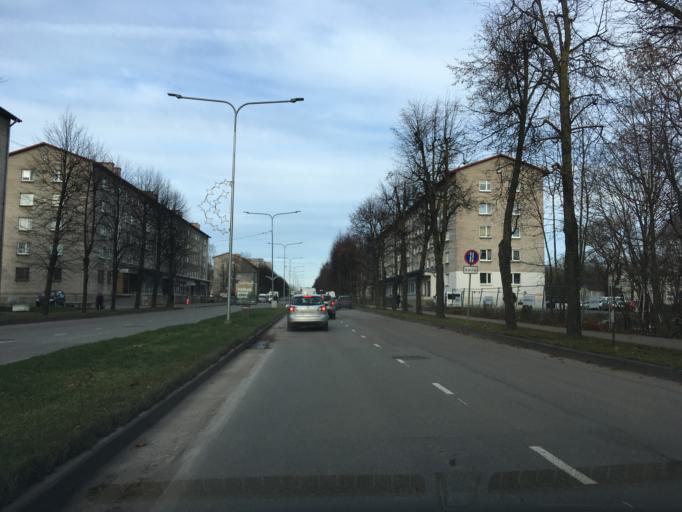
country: EE
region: Ida-Virumaa
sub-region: Narva linn
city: Narva
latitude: 59.3747
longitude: 28.1821
